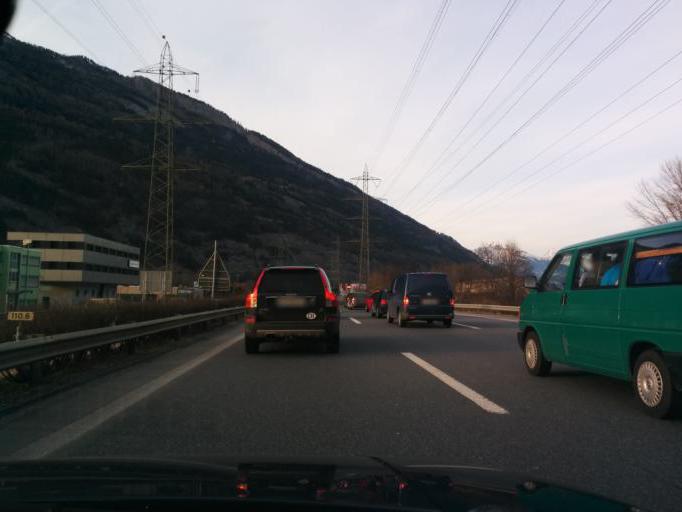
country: CH
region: Grisons
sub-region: Plessur District
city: Chur
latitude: 46.8515
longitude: 9.5065
